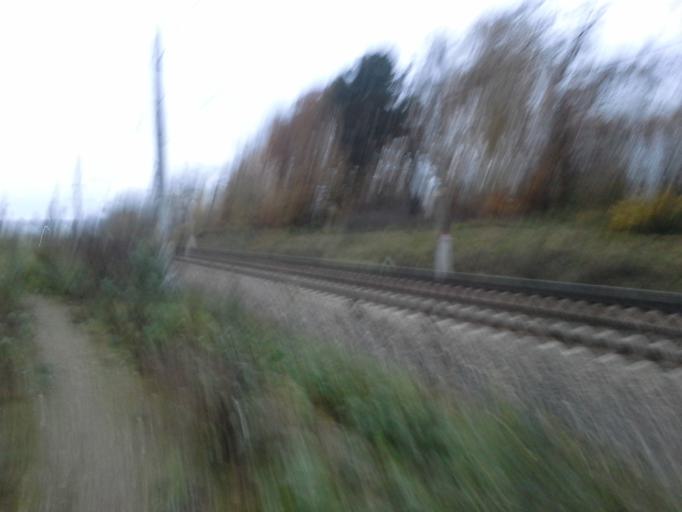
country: RU
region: Moskovskaya
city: Zhavoronki
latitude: 55.6418
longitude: 37.1084
